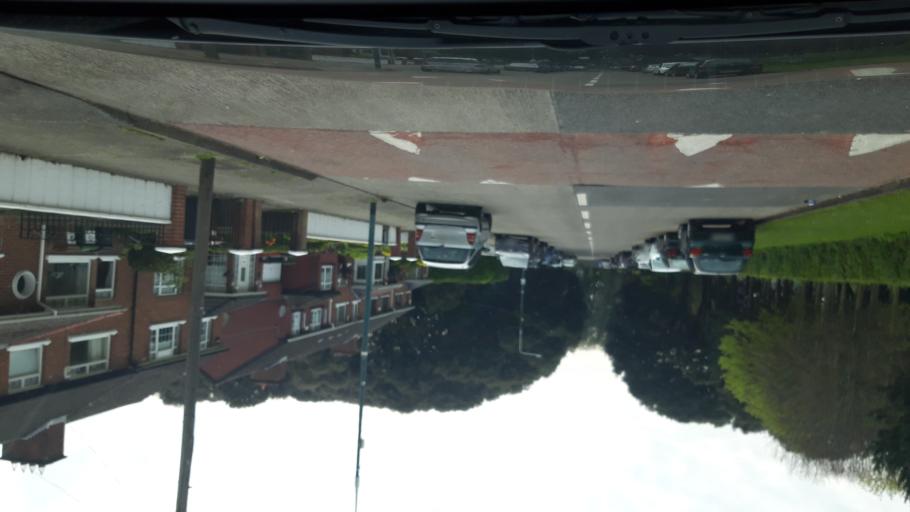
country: IE
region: Leinster
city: Dollymount
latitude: 53.3755
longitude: -6.1735
